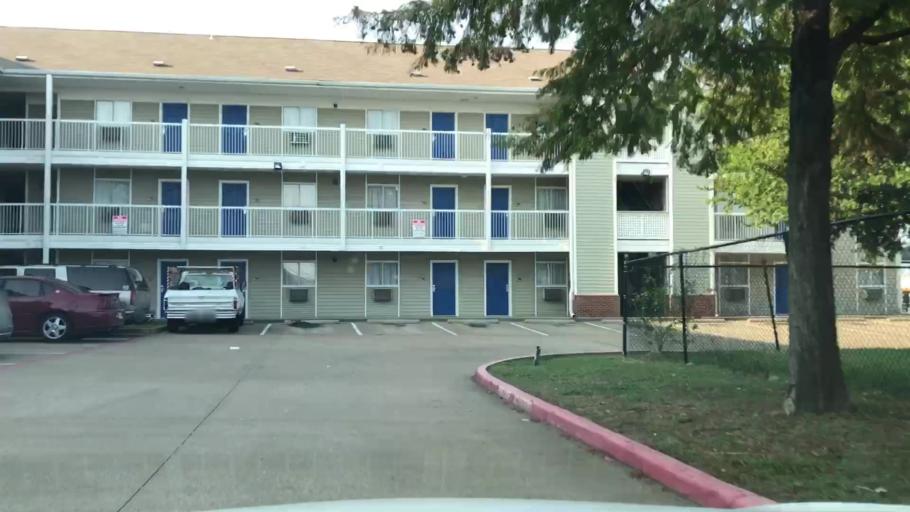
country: US
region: Texas
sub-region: Dallas County
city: Richardson
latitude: 32.9100
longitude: -96.7371
